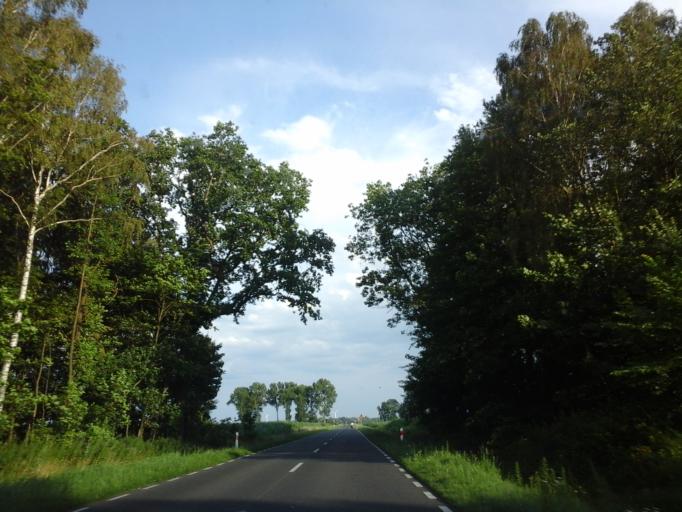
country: PL
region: West Pomeranian Voivodeship
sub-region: Powiat kamienski
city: Kamien Pomorski
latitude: 53.9165
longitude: 14.8469
